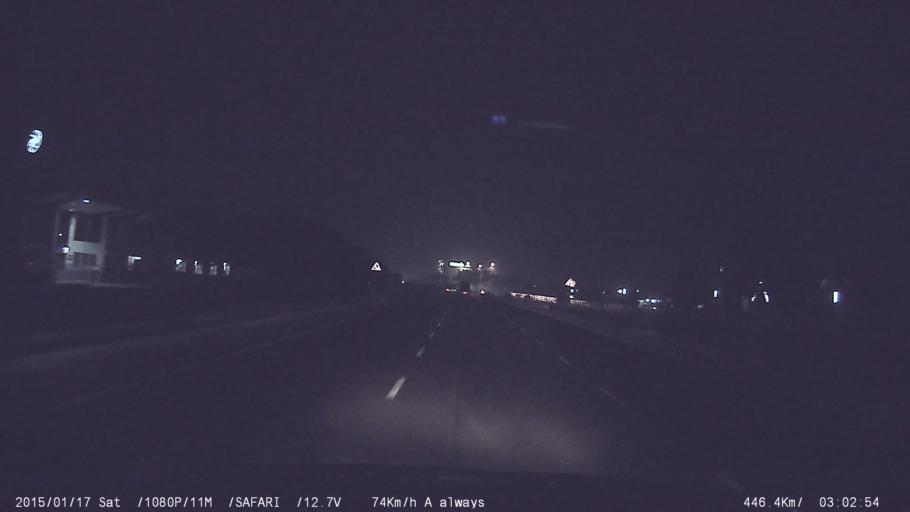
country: IN
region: Tamil Nadu
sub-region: Krishnagiri
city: Hosur
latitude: 12.7497
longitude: 77.8063
